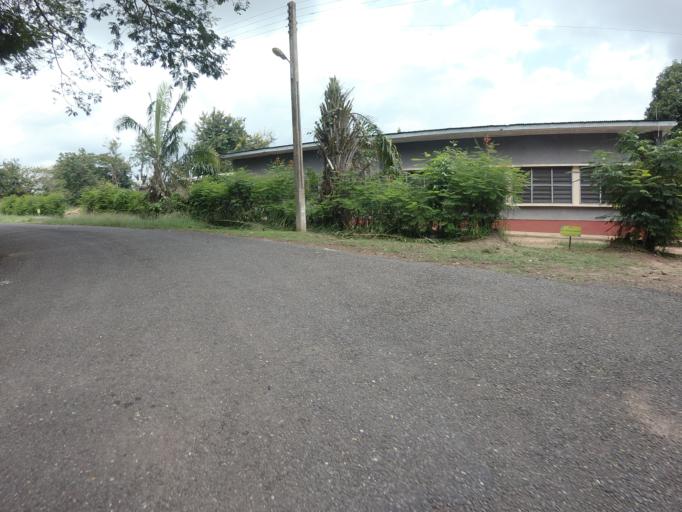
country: GH
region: Volta
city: Ho
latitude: 6.5959
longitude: 0.4744
